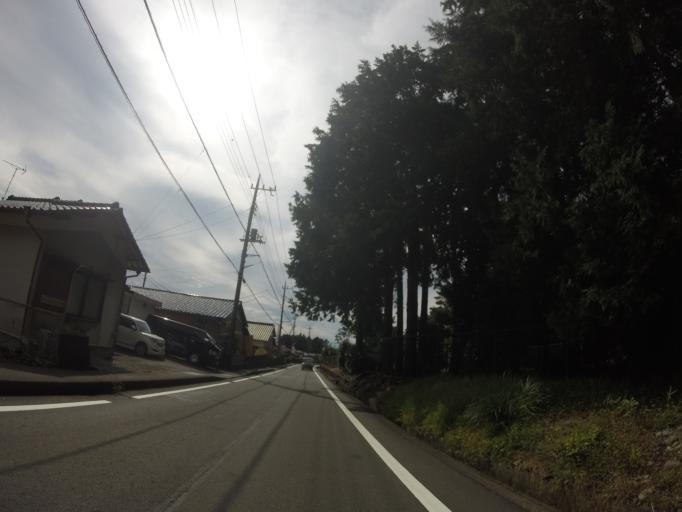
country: JP
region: Shizuoka
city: Fuji
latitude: 35.2076
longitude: 138.6706
